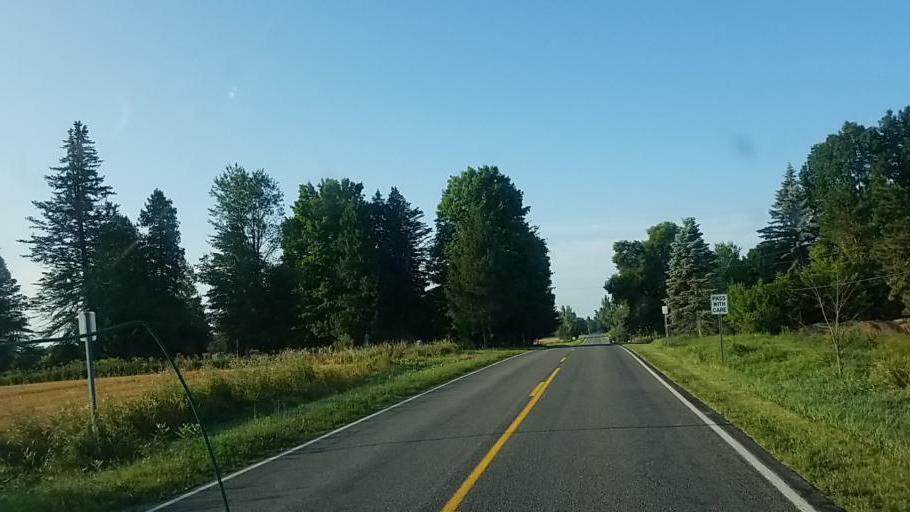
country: US
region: Michigan
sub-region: Montcalm County
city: Greenville
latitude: 43.2690
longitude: -85.3022
